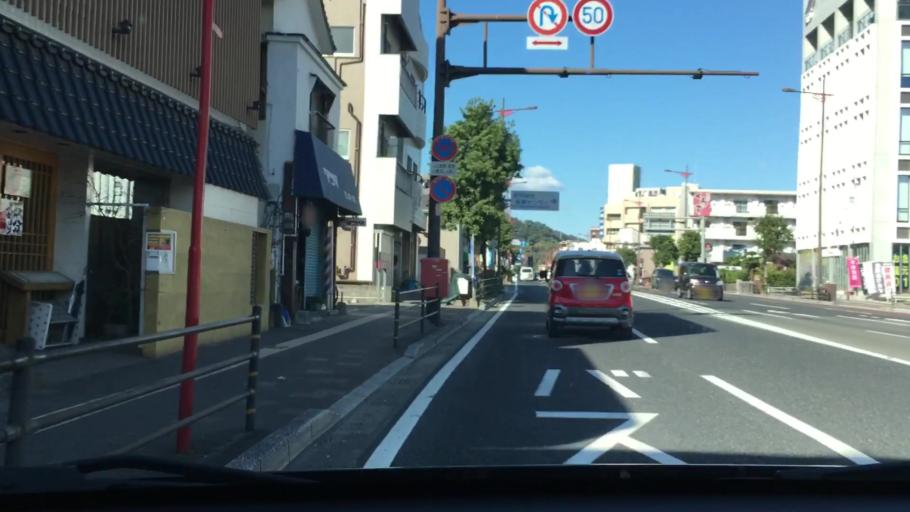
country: JP
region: Kagoshima
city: Kagoshima-shi
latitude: 31.6150
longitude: 130.5299
